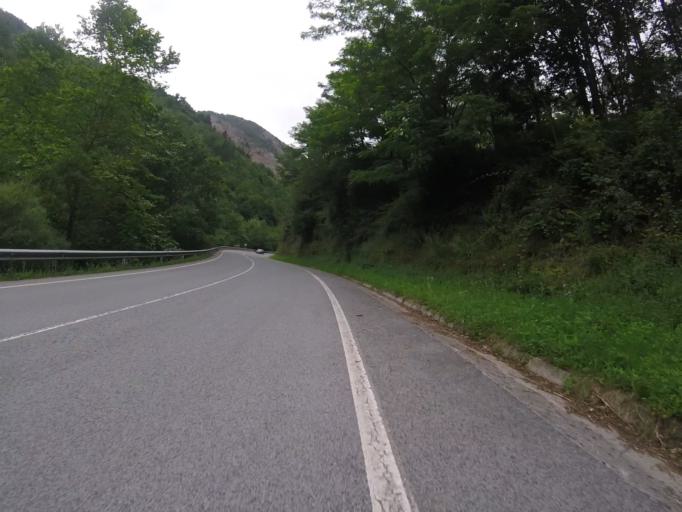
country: ES
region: Navarre
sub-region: Provincia de Navarra
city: Saldias
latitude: 43.1064
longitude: -1.7670
